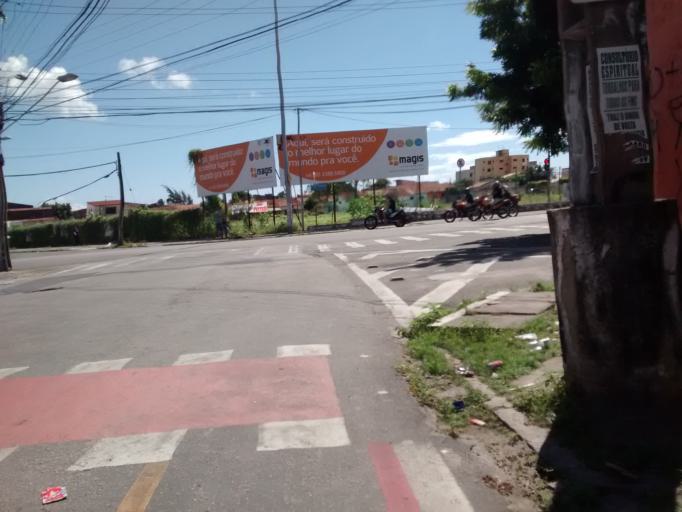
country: BR
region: Ceara
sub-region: Fortaleza
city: Fortaleza
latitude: -3.7202
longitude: -38.5496
